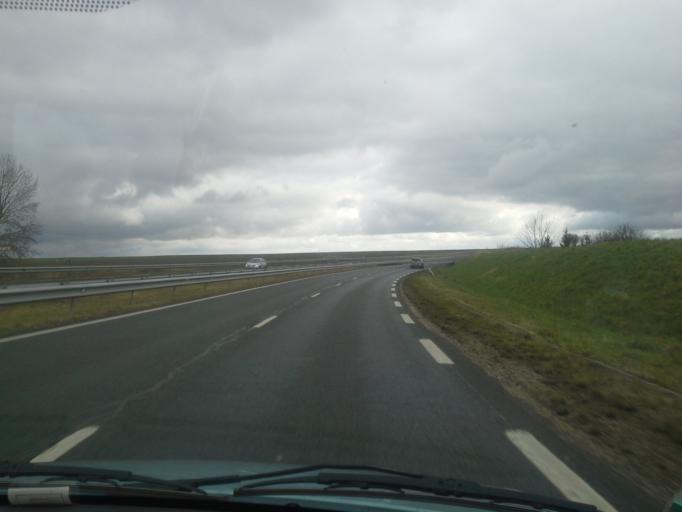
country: FR
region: Centre
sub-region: Departement du Loir-et-Cher
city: Vendome
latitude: 47.7336
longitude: 1.1467
